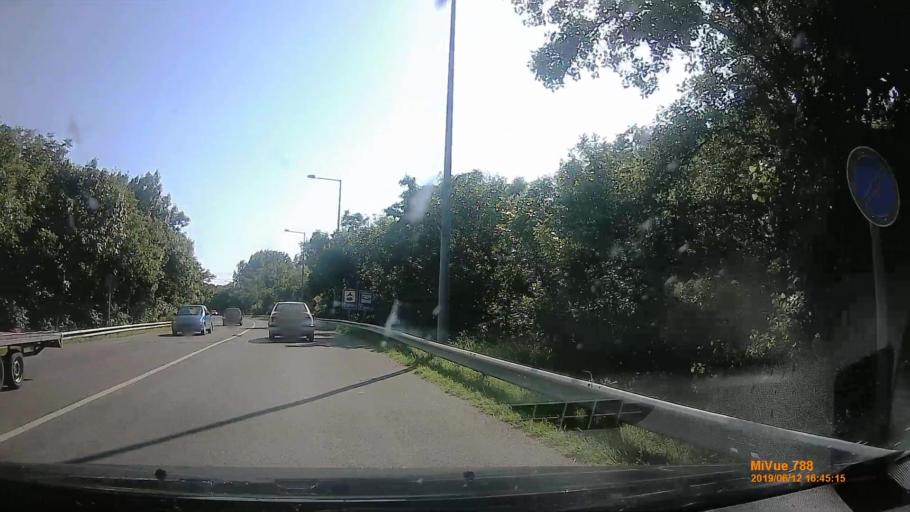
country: HU
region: Csongrad
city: Mako
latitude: 46.2095
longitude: 20.4603
